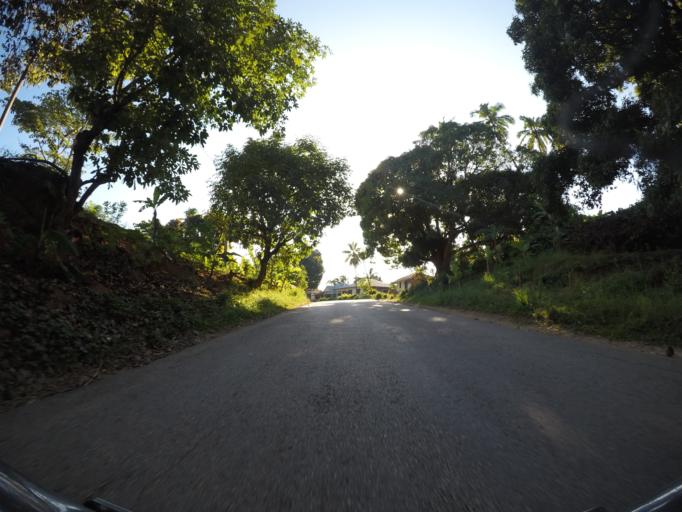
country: TZ
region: Pemba South
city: Chake Chake
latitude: -5.2793
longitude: 39.7674
